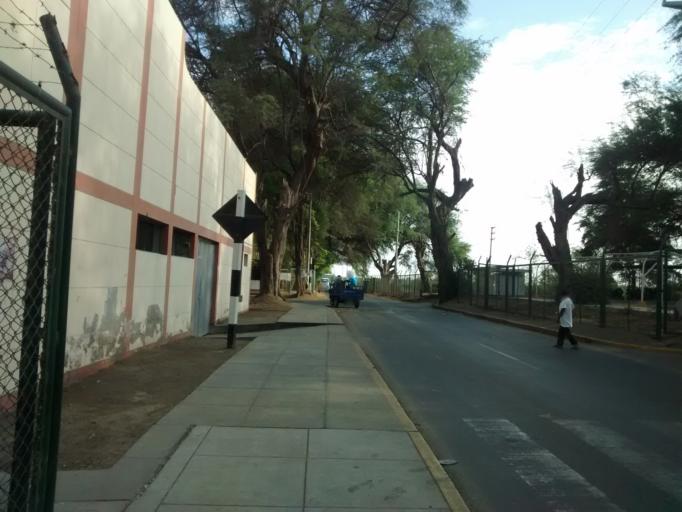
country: PE
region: Piura
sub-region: Provincia de Piura
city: Piura
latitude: -5.1777
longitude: -80.6196
